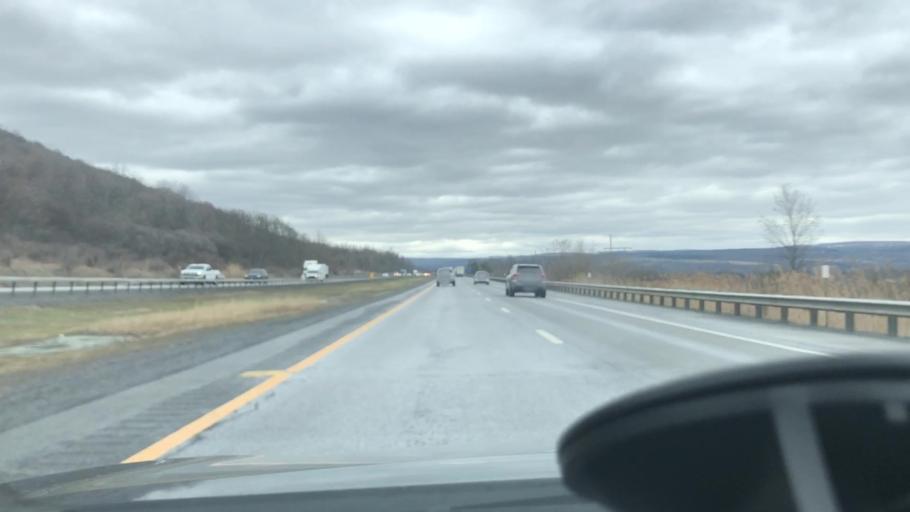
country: US
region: New York
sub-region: Herkimer County
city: Frankfort
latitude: 43.0432
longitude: -75.0550
